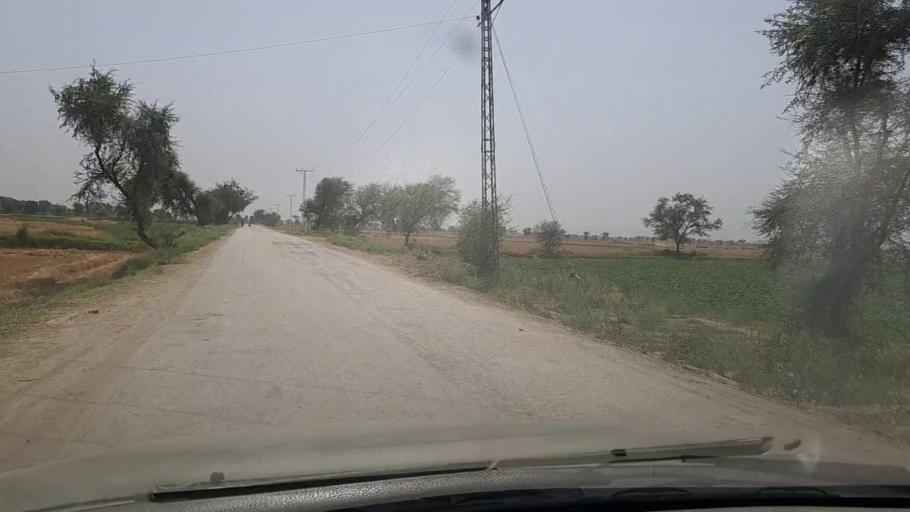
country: PK
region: Sindh
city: Miro Khan
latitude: 27.7164
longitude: 68.0671
